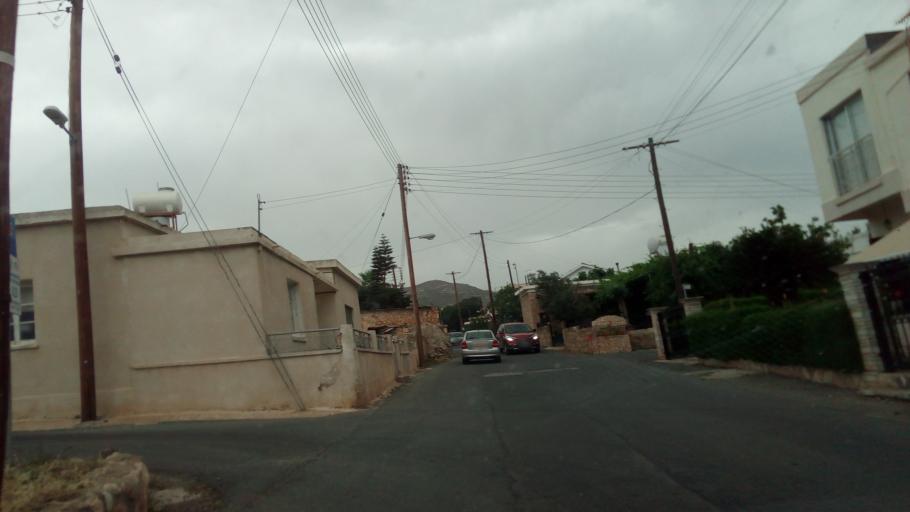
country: CY
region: Pafos
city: Mesogi
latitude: 34.8182
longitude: 32.4466
